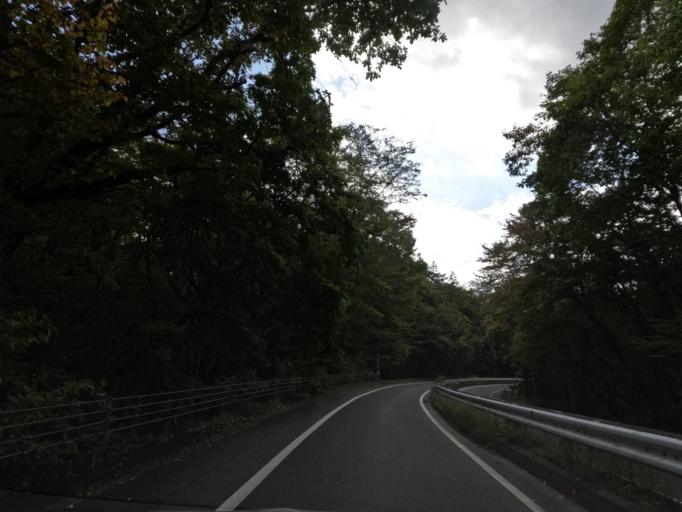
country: JP
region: Hokkaido
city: Chitose
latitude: 42.8051
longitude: 141.5845
